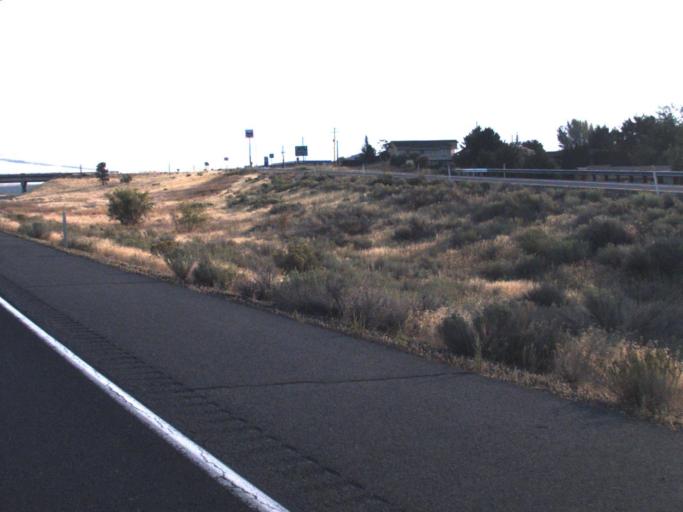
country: US
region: Washington
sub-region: Yakima County
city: Selah
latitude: 46.6752
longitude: -120.4836
